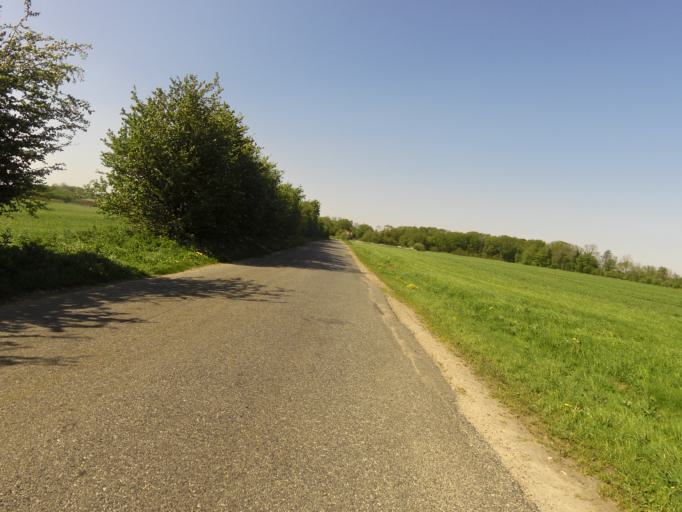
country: DK
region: South Denmark
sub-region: Tonder Kommune
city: Sherrebek
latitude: 55.2171
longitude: 8.8484
